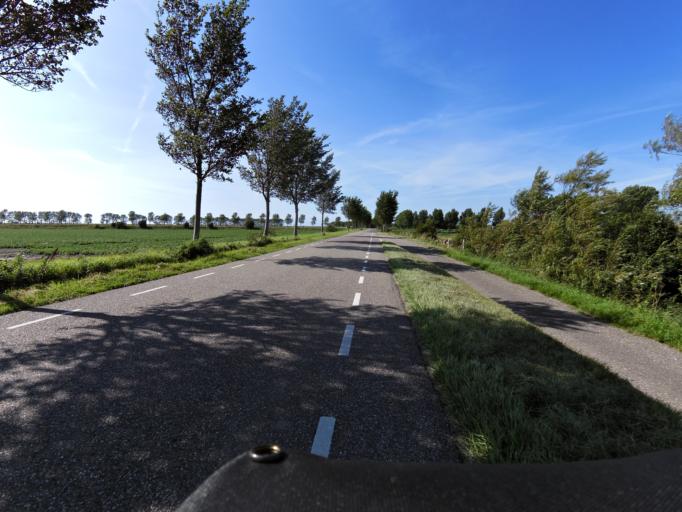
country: NL
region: South Holland
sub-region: Gemeente Goeree-Overflakkee
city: Dirksland
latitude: 51.7313
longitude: 4.0720
